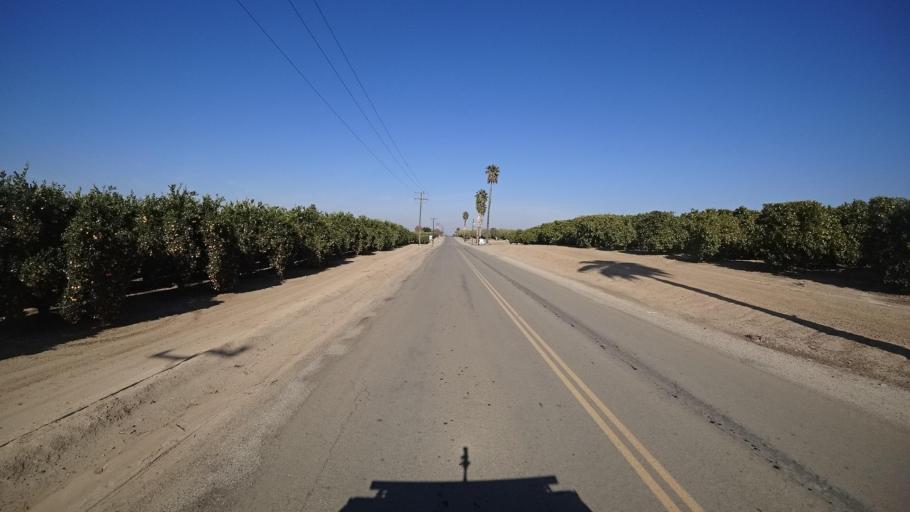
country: US
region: California
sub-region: Tulare County
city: Richgrove
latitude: 35.7137
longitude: -119.1339
